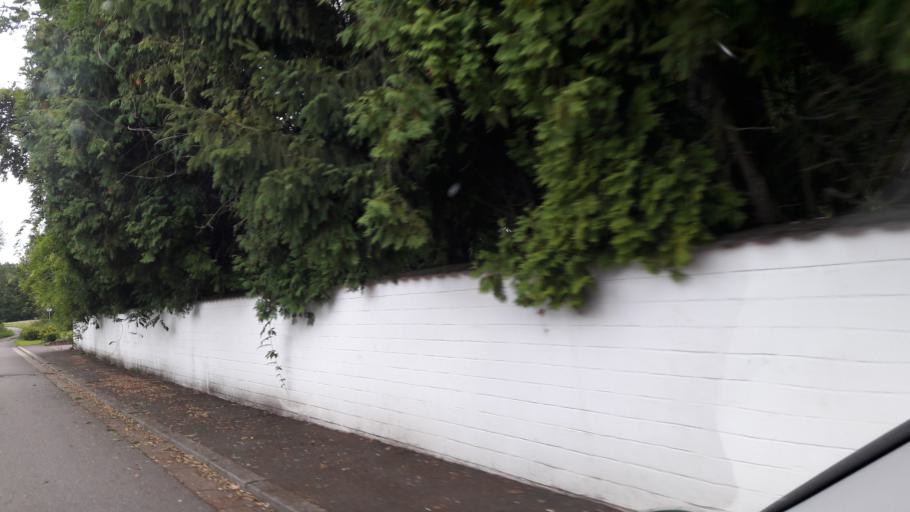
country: DE
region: Saarland
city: Tholey
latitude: 49.4601
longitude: 7.0054
